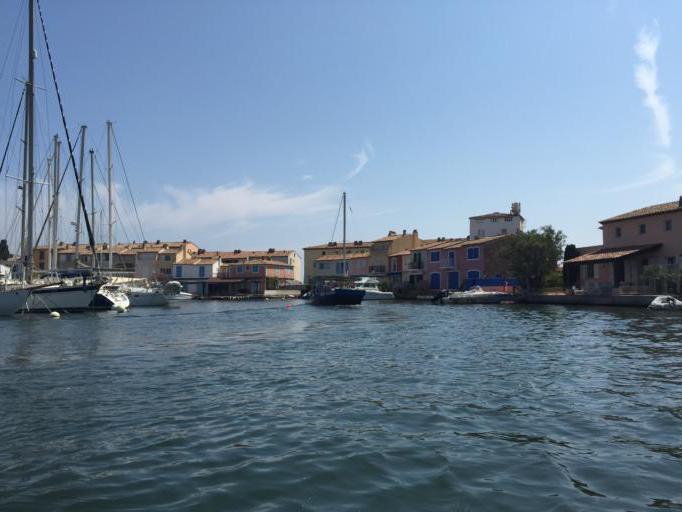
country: FR
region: Provence-Alpes-Cote d'Azur
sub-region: Departement du Var
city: Gassin
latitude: 43.2727
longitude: 6.5824
